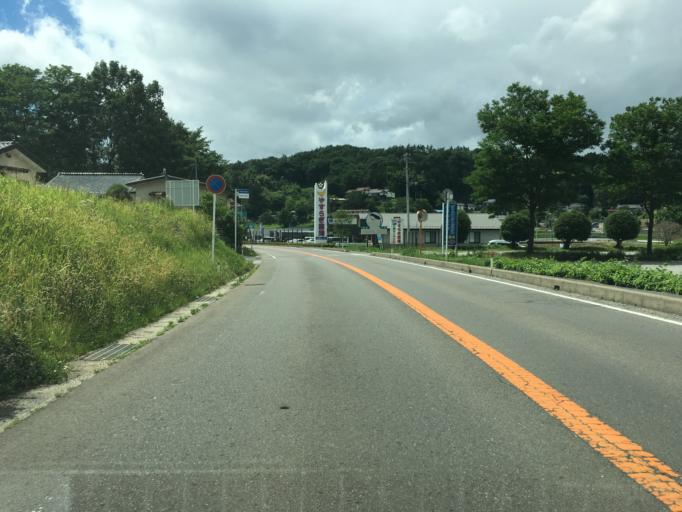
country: JP
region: Fukushima
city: Fukushima-shi
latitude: 37.6738
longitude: 140.5642
